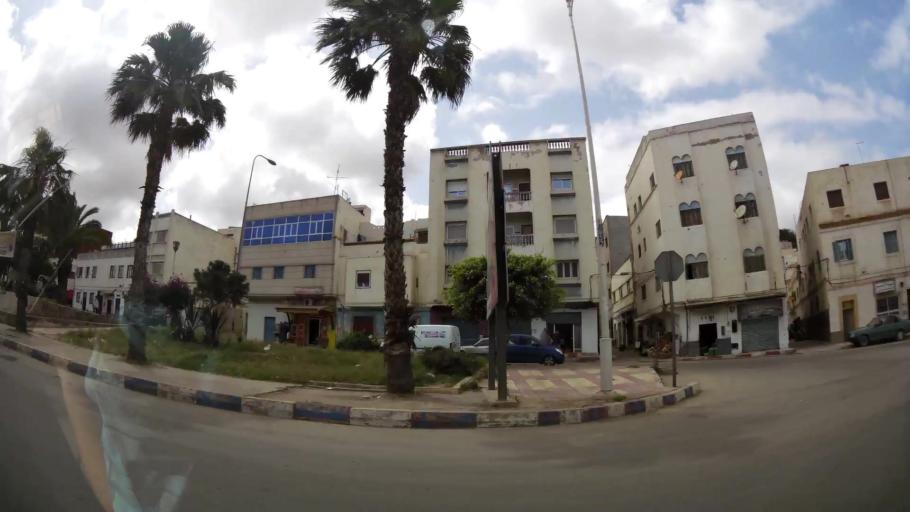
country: MA
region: Oriental
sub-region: Nador
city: Nador
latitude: 35.1774
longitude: -2.9310
